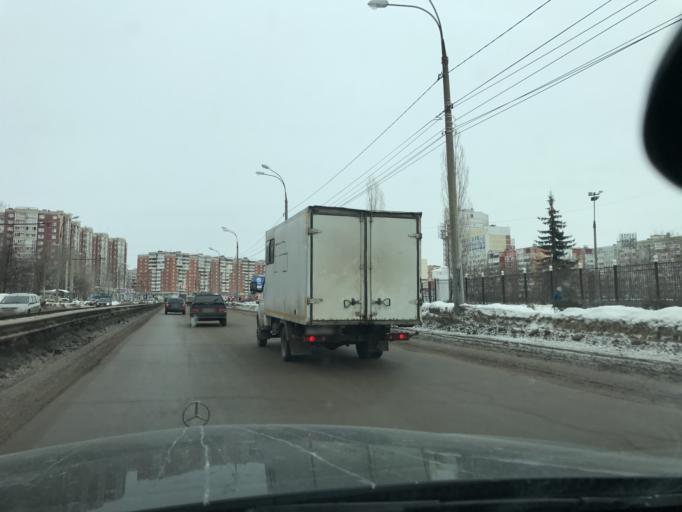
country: RU
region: Nizjnij Novgorod
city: Gorbatovka
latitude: 56.2556
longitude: 43.8532
